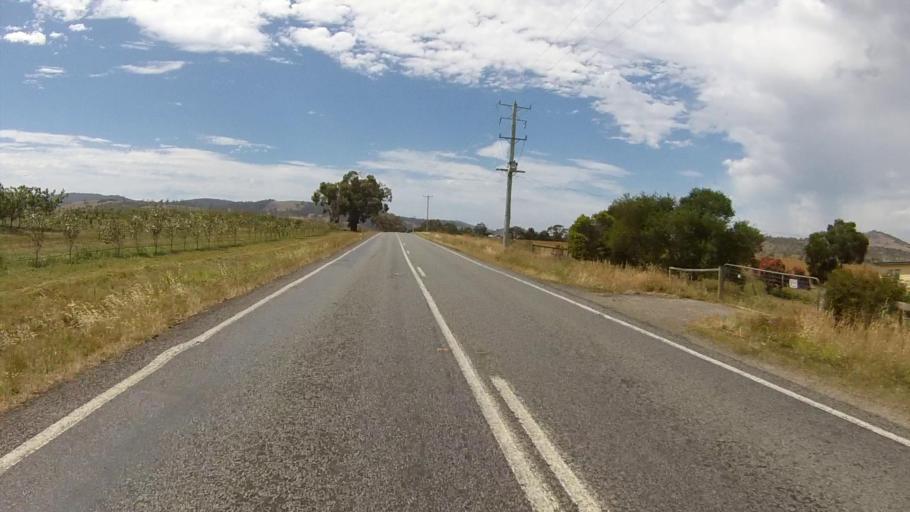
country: AU
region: Tasmania
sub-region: Clarence
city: Cambridge
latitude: -42.6885
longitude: 147.4459
